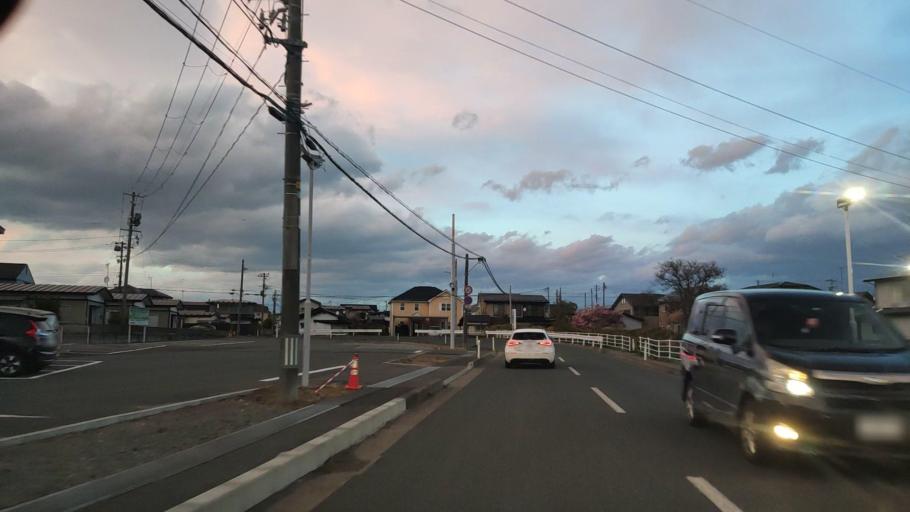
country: JP
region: Iwate
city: Morioka-shi
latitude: 39.7160
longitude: 141.1105
